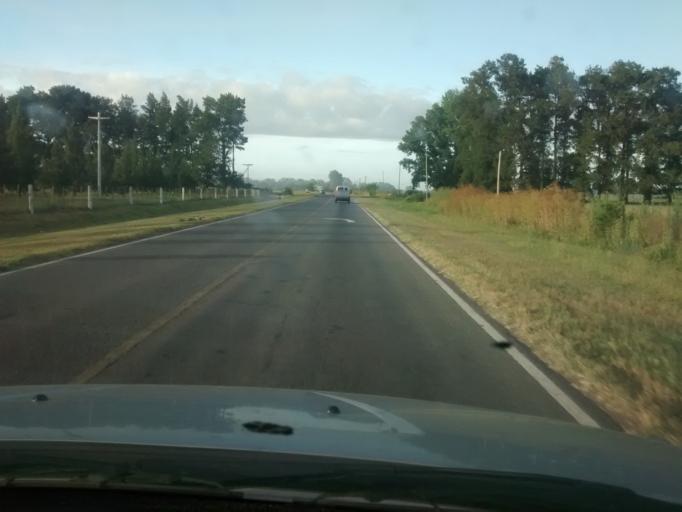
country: AR
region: Buenos Aires
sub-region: Partido de Brandsen
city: Brandsen
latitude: -35.1281
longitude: -58.1950
